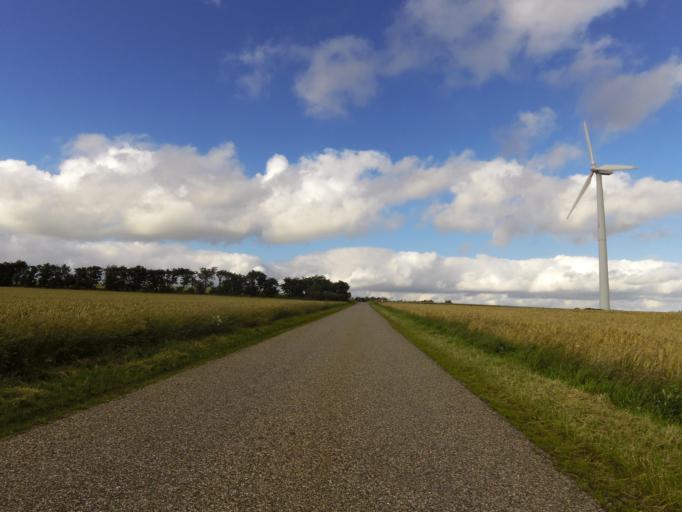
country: DK
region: South Denmark
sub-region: Tonder Kommune
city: Toftlund
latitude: 55.1411
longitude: 9.0805
